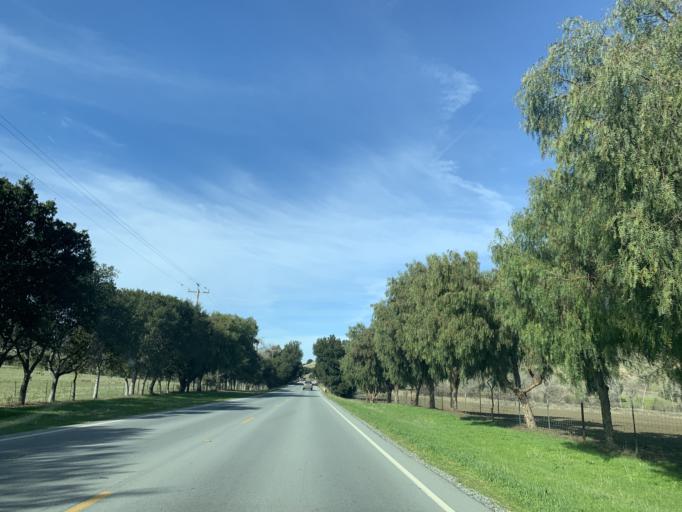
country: US
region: California
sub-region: San Benito County
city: Ridgemark
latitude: 36.7629
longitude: -121.2977
